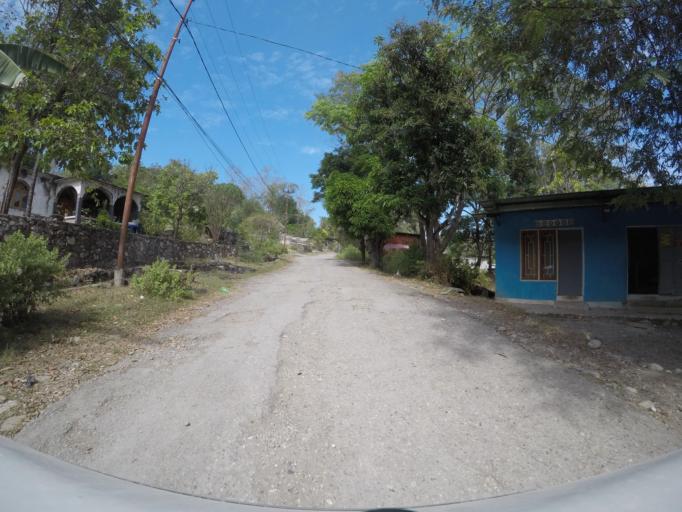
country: TL
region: Bobonaro
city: Maliana
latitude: -8.9939
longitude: 125.2249
